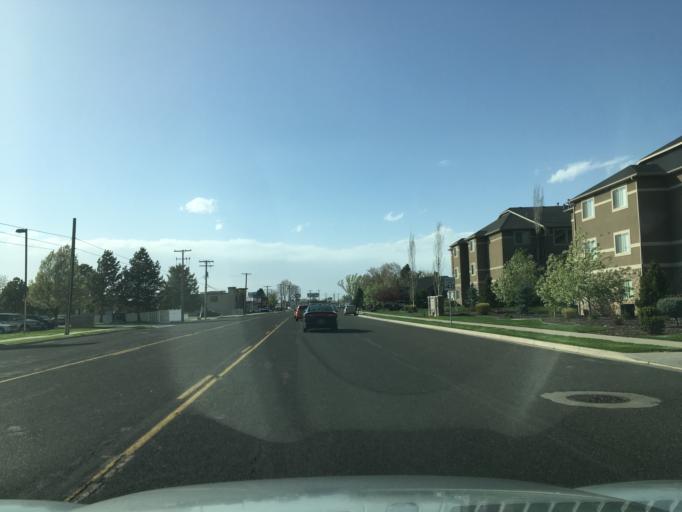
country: US
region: Utah
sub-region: Davis County
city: Kaysville
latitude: 41.0464
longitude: -111.9532
